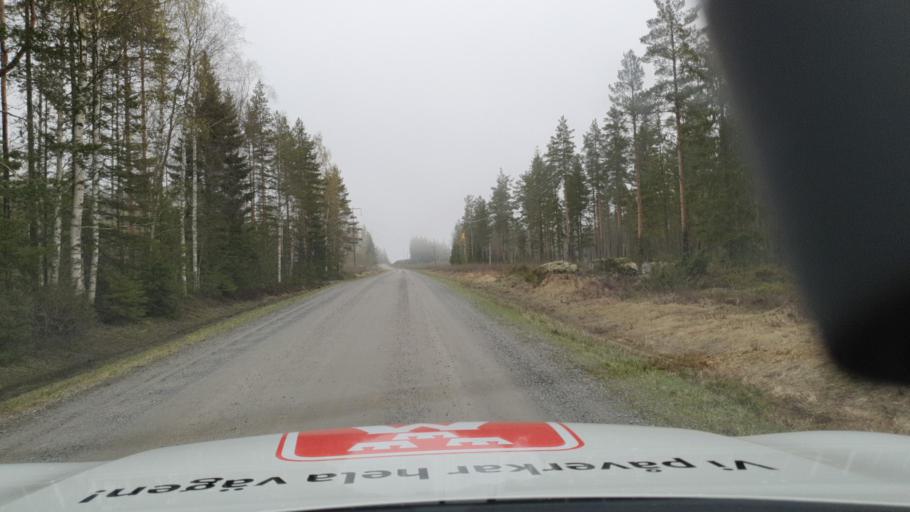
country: SE
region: Vaesterbotten
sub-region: Nordmalings Kommun
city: Nordmaling
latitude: 63.7470
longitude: 19.5003
